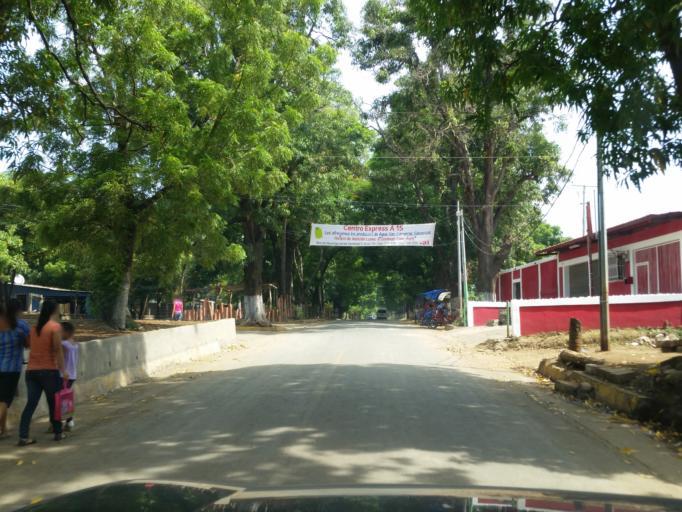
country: NI
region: Managua
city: Masachapa
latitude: 11.7883
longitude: -86.5130
